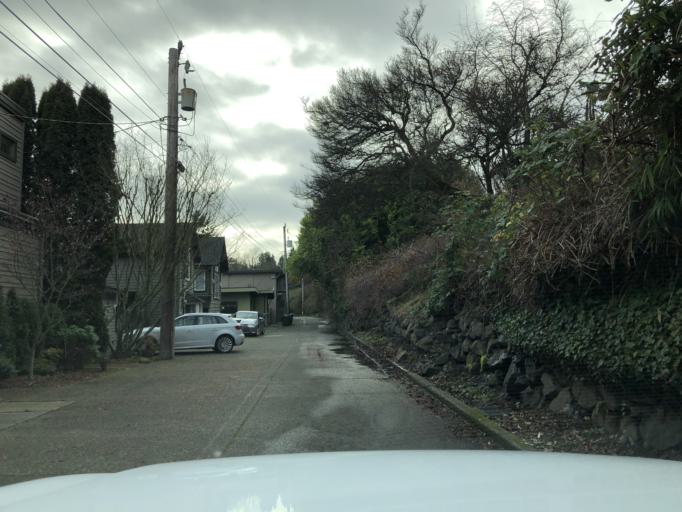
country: US
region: Washington
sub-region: King County
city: Inglewood-Finn Hill
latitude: 47.7070
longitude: -122.2753
